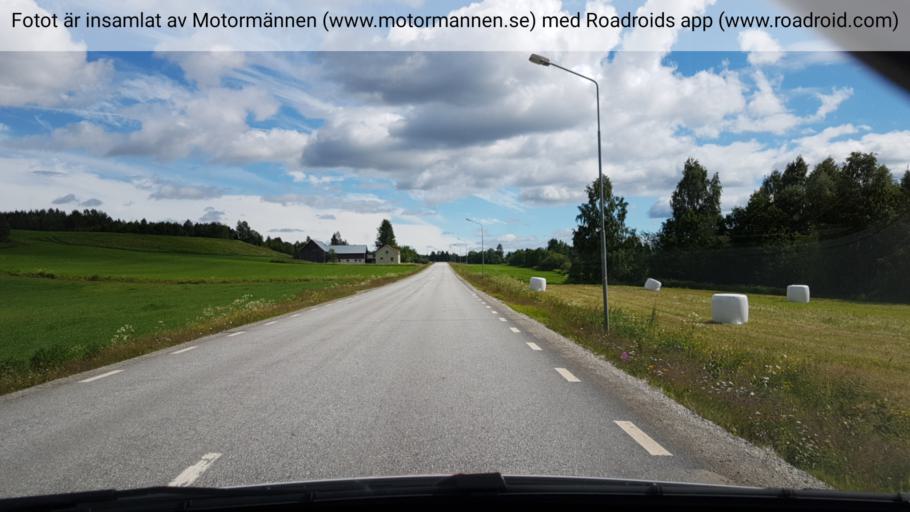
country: SE
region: Vaesterbotten
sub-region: Vindelns Kommun
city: Vindeln
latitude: 64.1726
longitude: 19.4867
